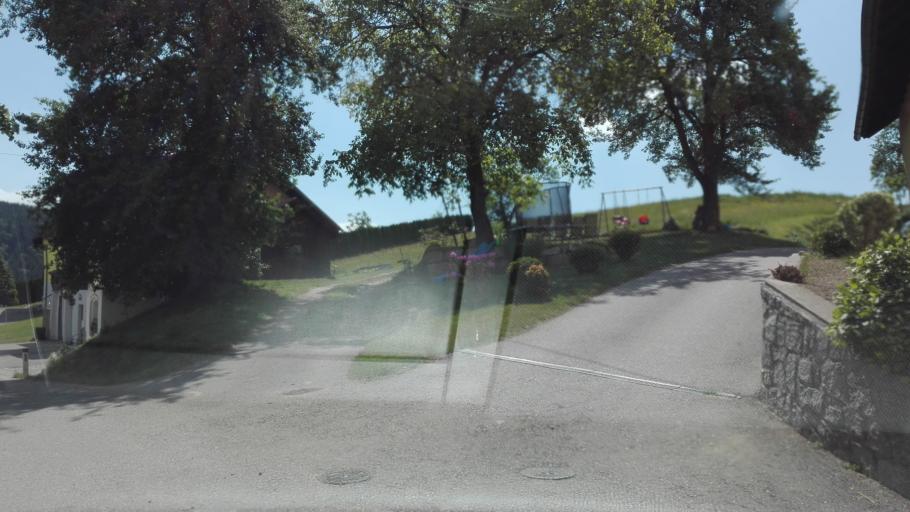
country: AT
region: Upper Austria
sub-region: Politischer Bezirk Rohrbach
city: Atzesberg
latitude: 48.4100
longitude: 13.8950
